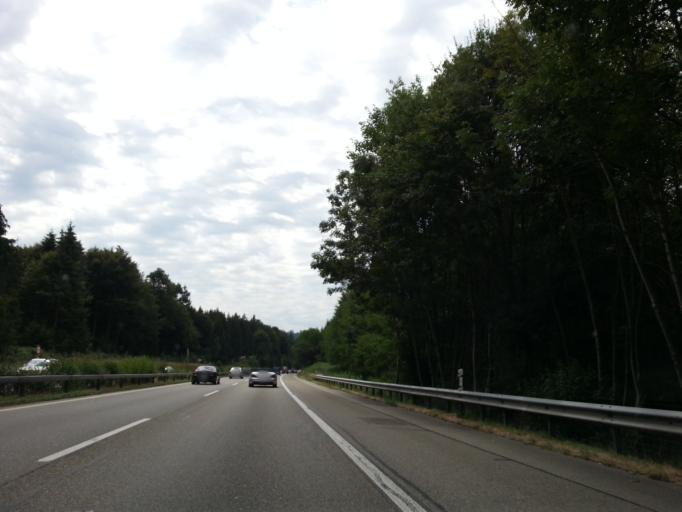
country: CH
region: Bern
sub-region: Emmental District
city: Hindelbank
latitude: 47.0363
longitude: 7.5286
